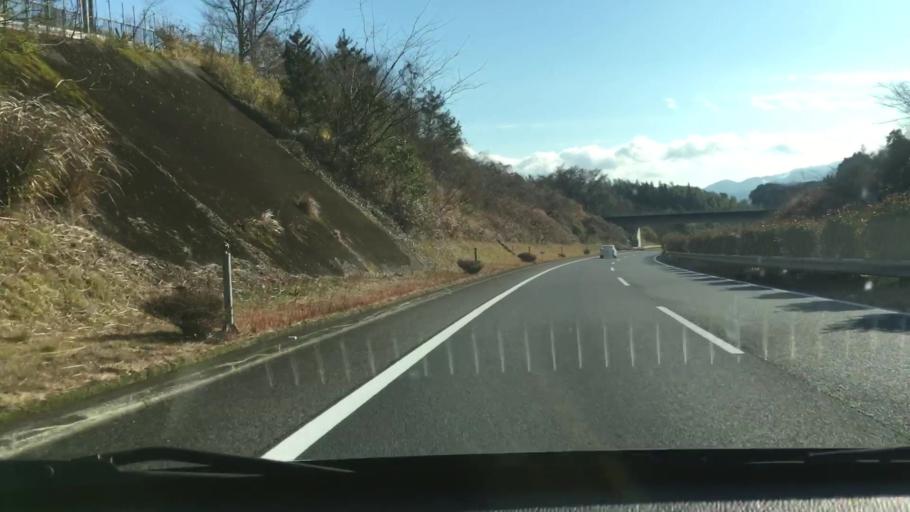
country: JP
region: Kumamoto
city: Hitoyoshi
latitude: 32.2203
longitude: 130.7803
